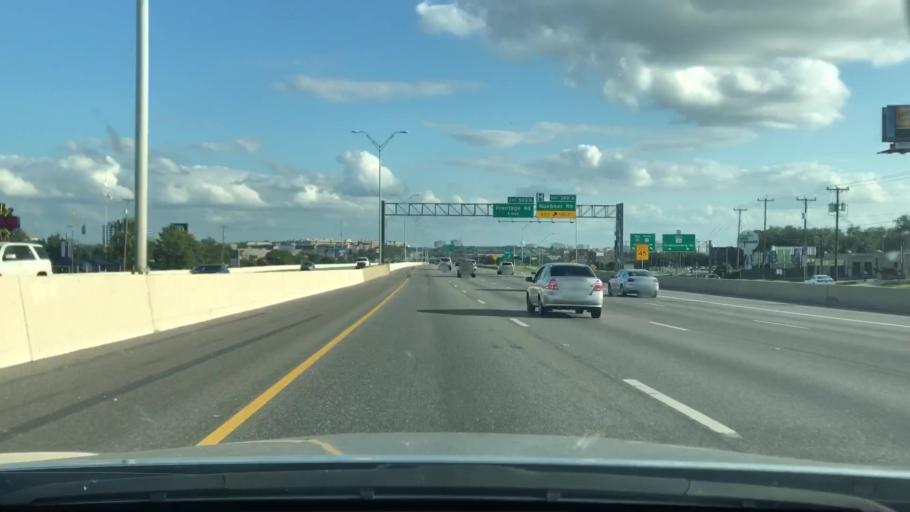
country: US
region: Texas
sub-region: Bexar County
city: Shavano Park
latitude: 29.5541
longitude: -98.5874
